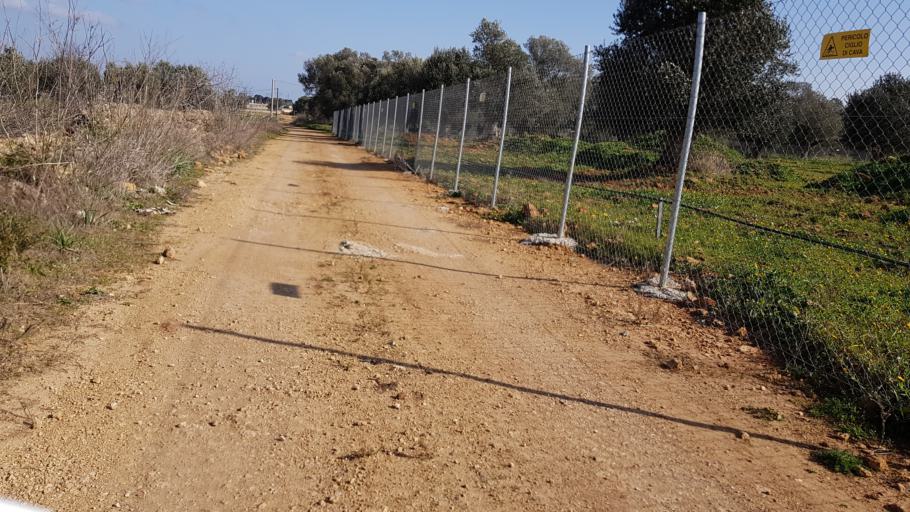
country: IT
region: Apulia
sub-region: Provincia di Brindisi
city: Mesagne
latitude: 40.5915
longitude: 17.8696
